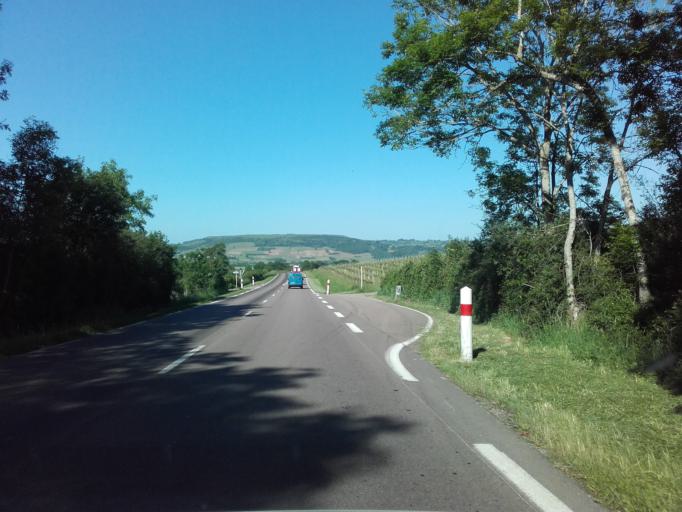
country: FR
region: Bourgogne
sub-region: Departement de la Cote-d'Or
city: Nolay
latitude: 46.9439
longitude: 4.6639
